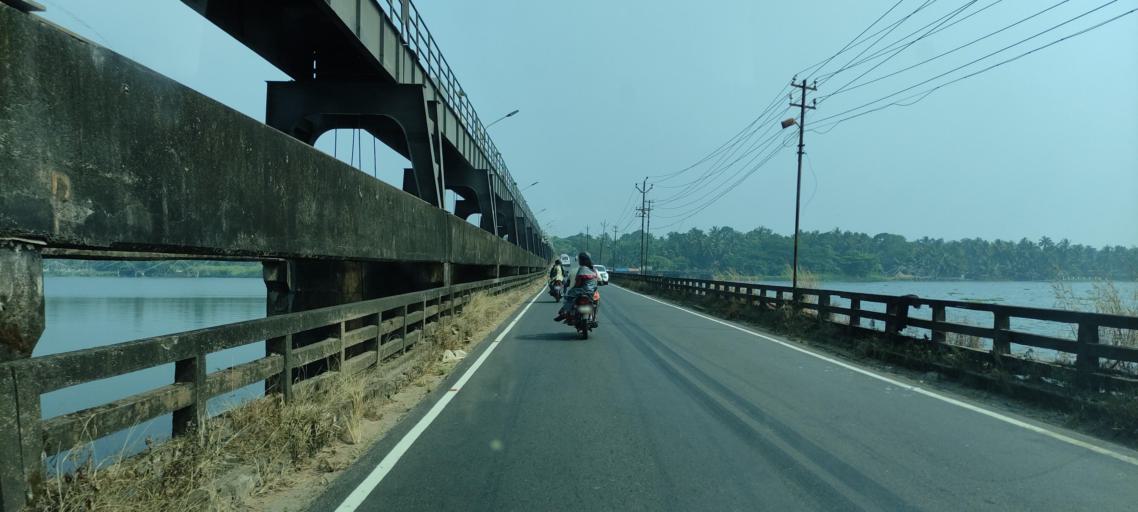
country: IN
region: Kerala
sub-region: Alappuzha
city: Shertallai
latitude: 9.6730
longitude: 76.4033
